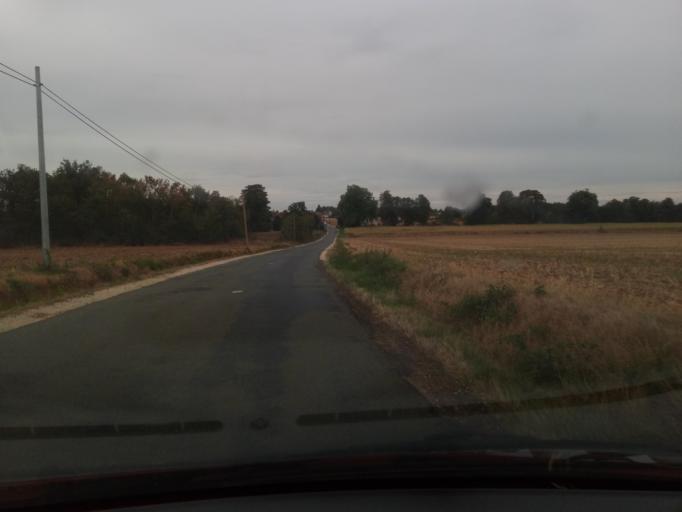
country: FR
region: Poitou-Charentes
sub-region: Departement de la Vienne
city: Saint-Savin
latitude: 46.5161
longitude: 0.7742
